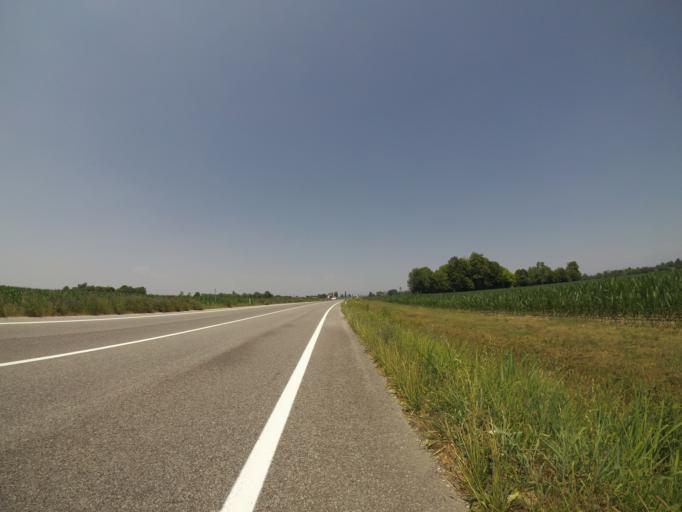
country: IT
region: Friuli Venezia Giulia
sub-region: Provincia di Udine
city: Varmo
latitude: 45.8987
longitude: 13.0068
